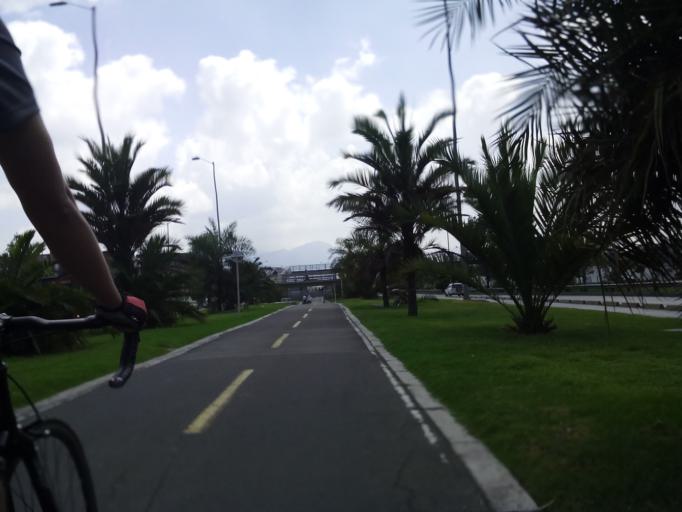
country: CO
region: Bogota D.C.
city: Bogota
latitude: 4.6704
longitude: -74.1142
